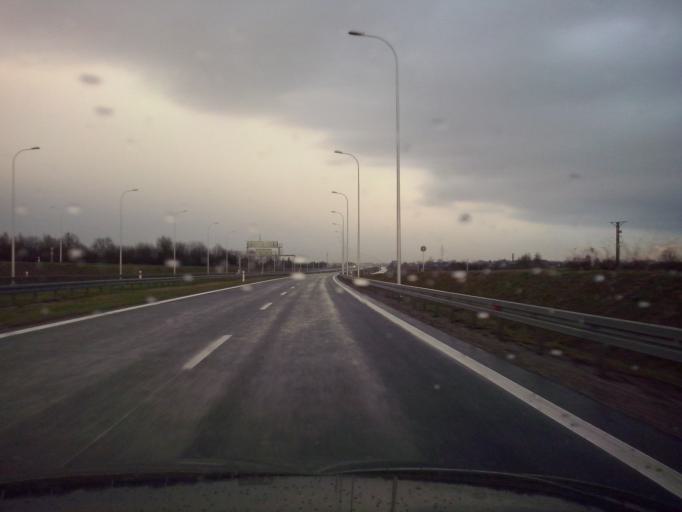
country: PL
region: Lublin Voivodeship
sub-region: Powiat lubelski
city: Jastkow
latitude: 51.2768
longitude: 22.4722
